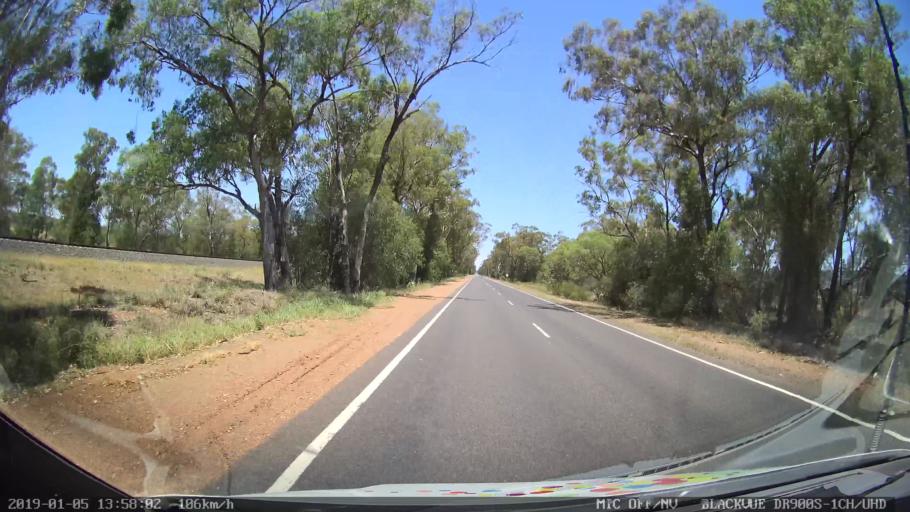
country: AU
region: New South Wales
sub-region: Gunnedah
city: Gunnedah
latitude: -31.1344
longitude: 150.2799
